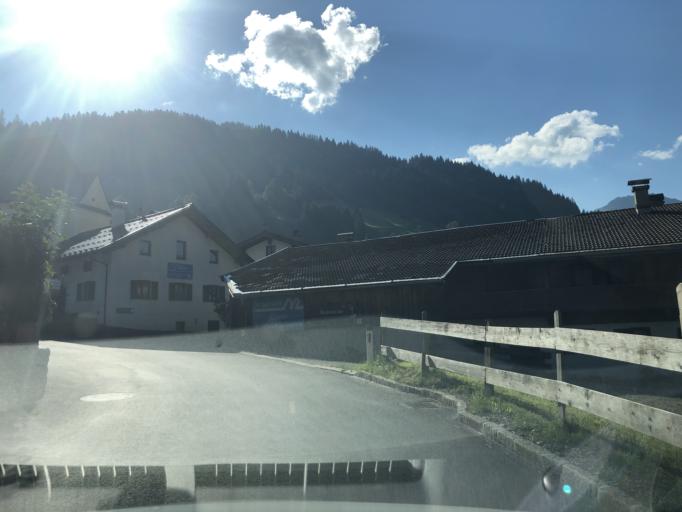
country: AT
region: Tyrol
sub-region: Politischer Bezirk Kitzbuhel
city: Kirchberg in Tirol
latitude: 47.3827
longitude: 12.3092
